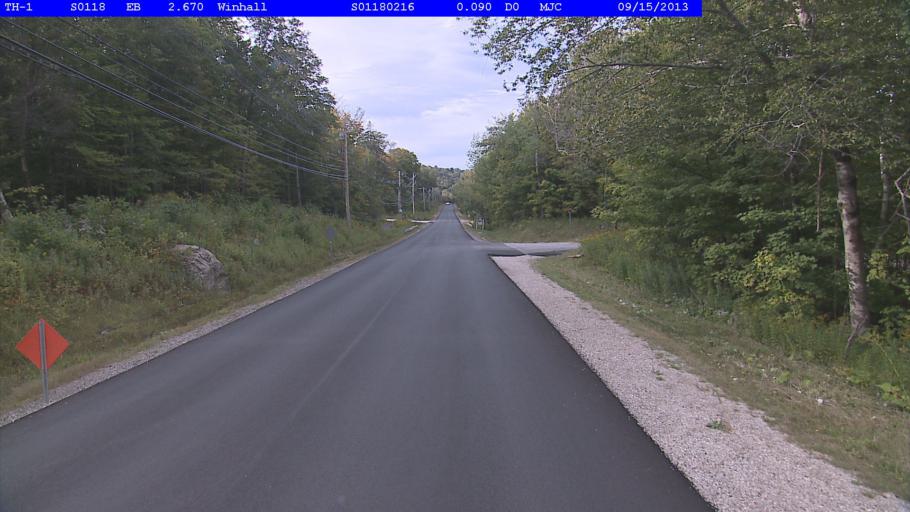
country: US
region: Vermont
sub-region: Bennington County
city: Manchester Center
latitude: 43.1166
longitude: -72.9100
